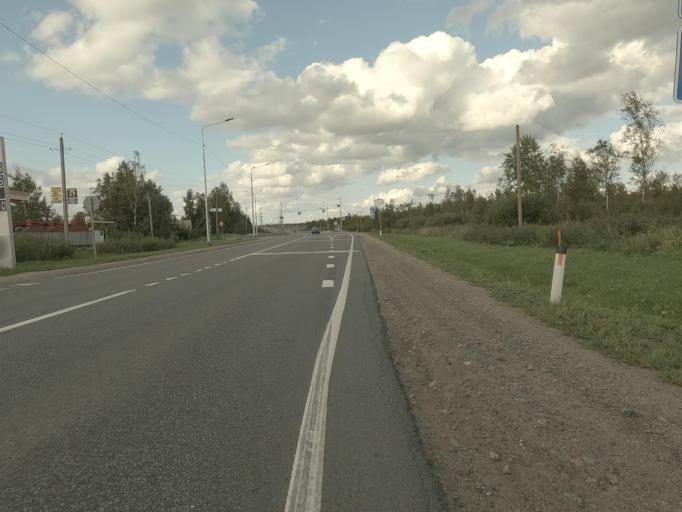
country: RU
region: Leningrad
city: Mga
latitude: 59.7455
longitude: 31.0844
